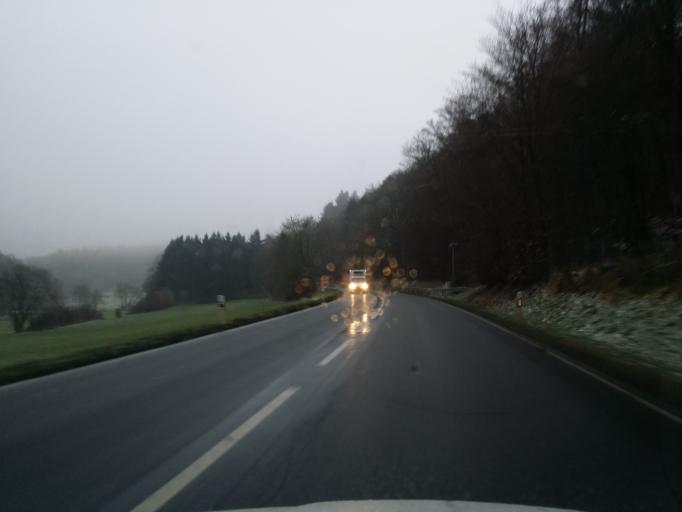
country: DE
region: Hesse
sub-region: Regierungsbezirk Darmstadt
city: Idstein
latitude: 50.1952
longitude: 8.2435
